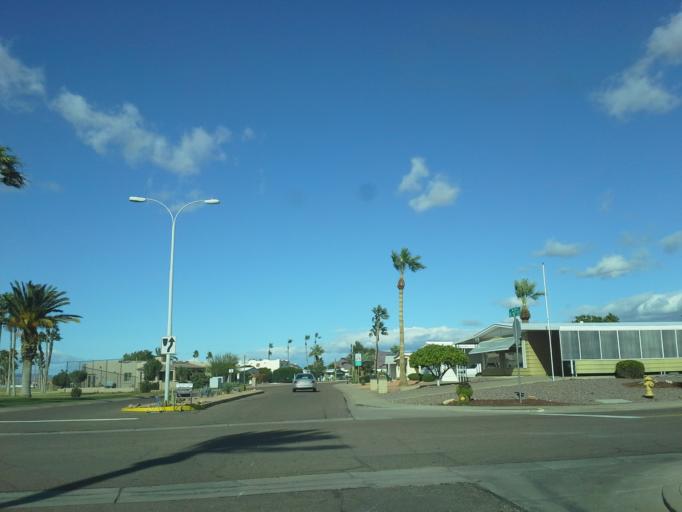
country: US
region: Arizona
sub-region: Maricopa County
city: Mesa
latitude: 33.4585
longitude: -111.7114
